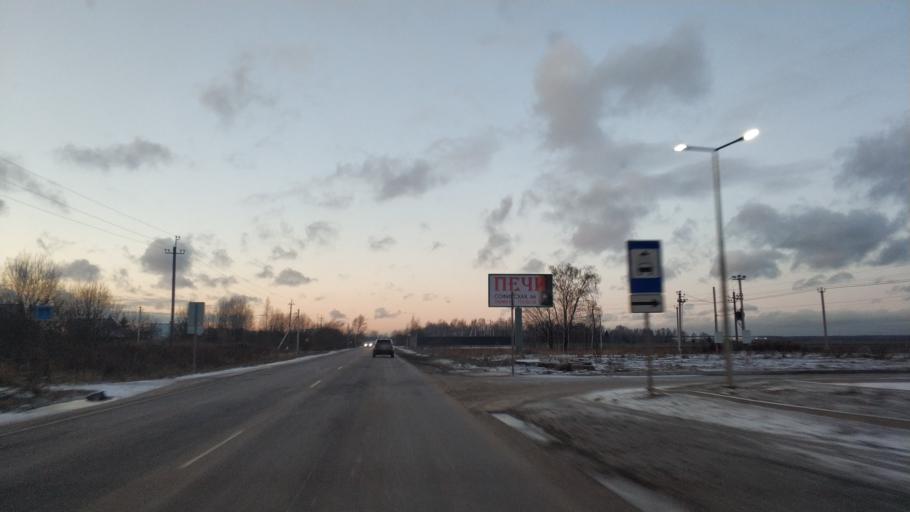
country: RU
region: St.-Petersburg
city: Pontonnyy
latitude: 59.8025
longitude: 30.6313
